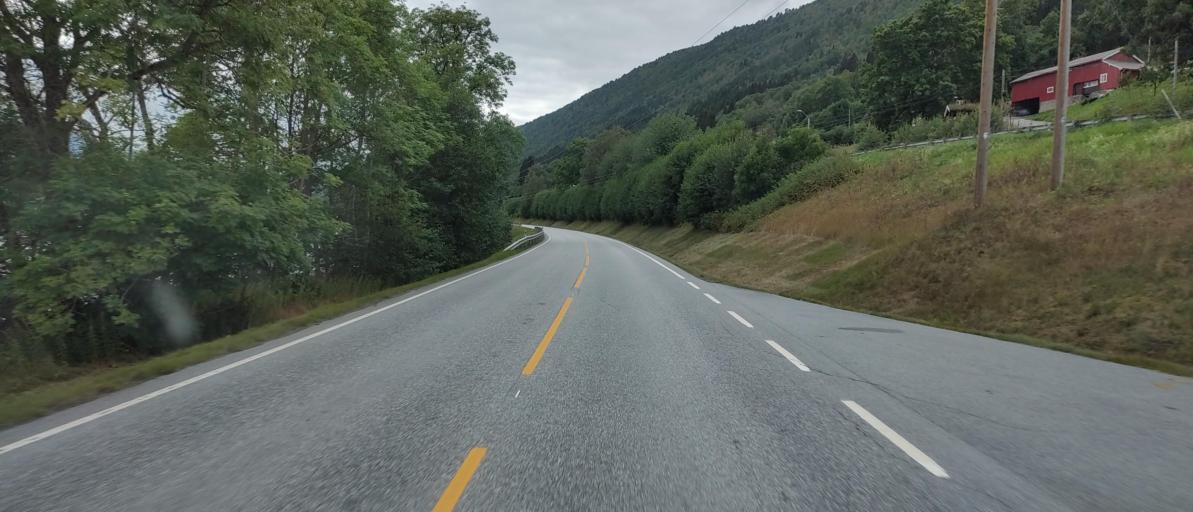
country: NO
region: More og Romsdal
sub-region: Rauma
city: Andalsnes
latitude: 62.5847
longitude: 7.7303
